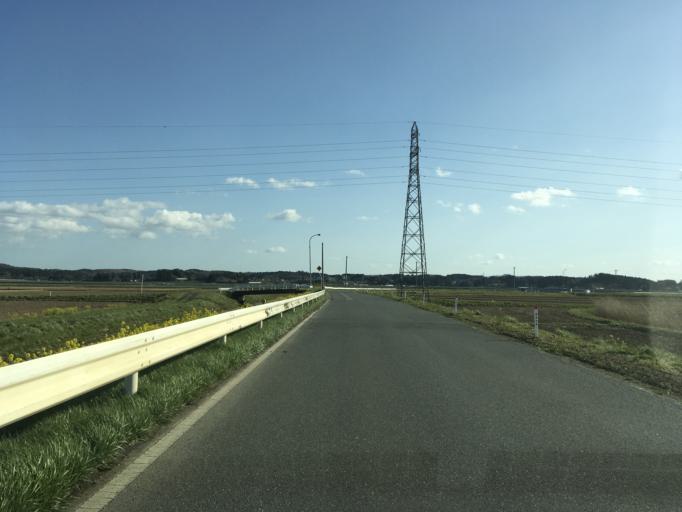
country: JP
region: Miyagi
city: Wakuya
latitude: 38.6572
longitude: 141.2384
